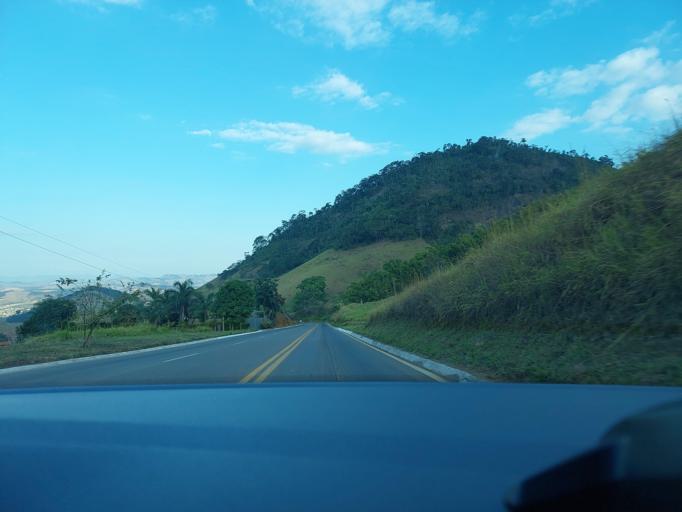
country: BR
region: Minas Gerais
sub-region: Muriae
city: Muriae
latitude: -21.0834
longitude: -42.4904
